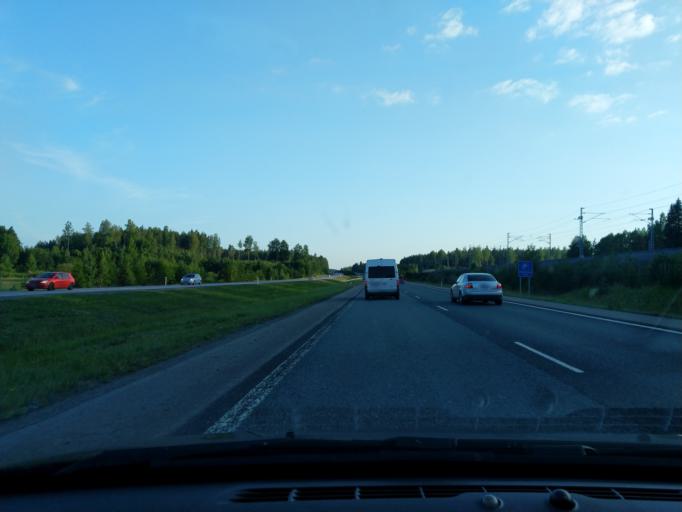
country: FI
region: Uusimaa
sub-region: Helsinki
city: Maentsaelae
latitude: 60.7050
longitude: 25.4114
